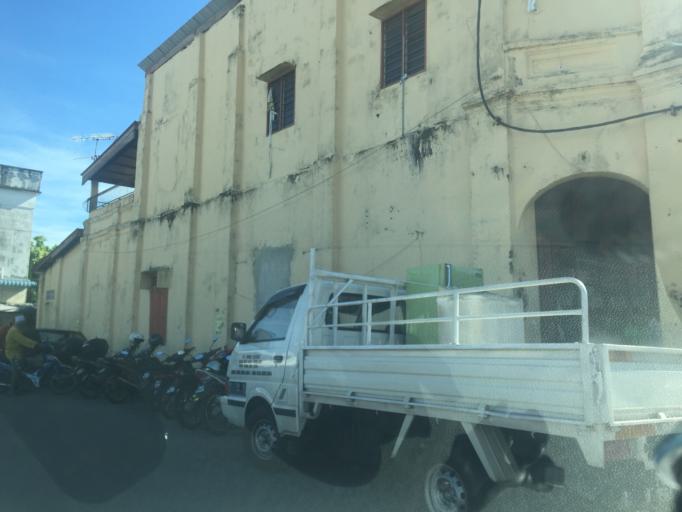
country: MY
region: Penang
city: Tasek Glugor
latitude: 5.5132
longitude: 100.5536
